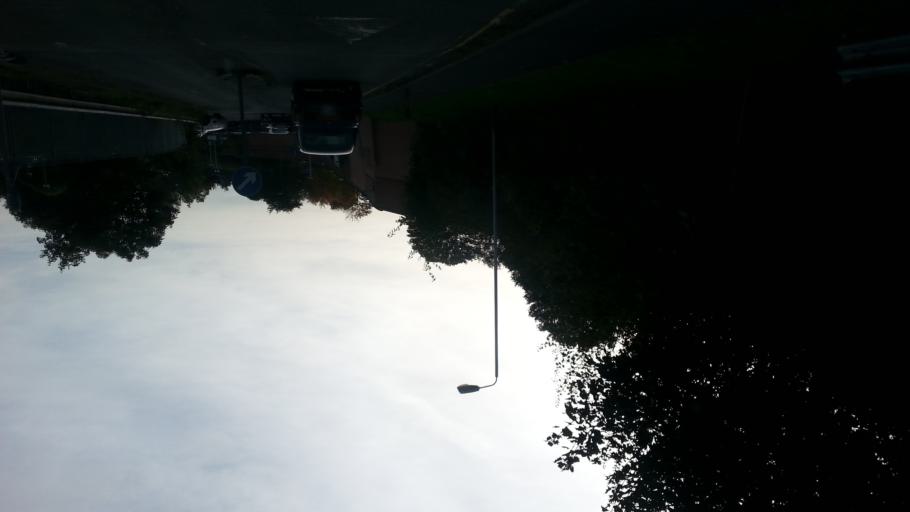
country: GB
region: England
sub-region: Northamptonshire
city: Northampton
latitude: 52.2389
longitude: -0.9054
